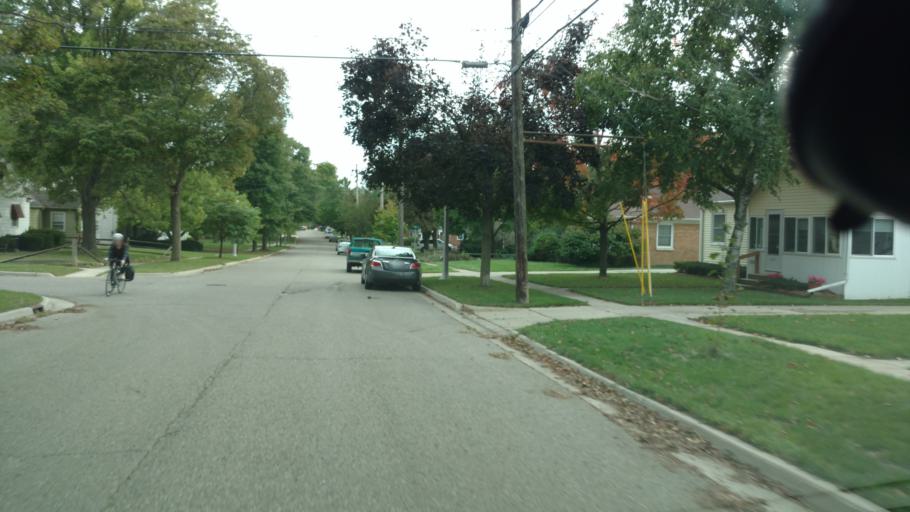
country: US
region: Michigan
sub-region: Ingham County
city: East Lansing
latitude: 42.7366
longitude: -84.5151
